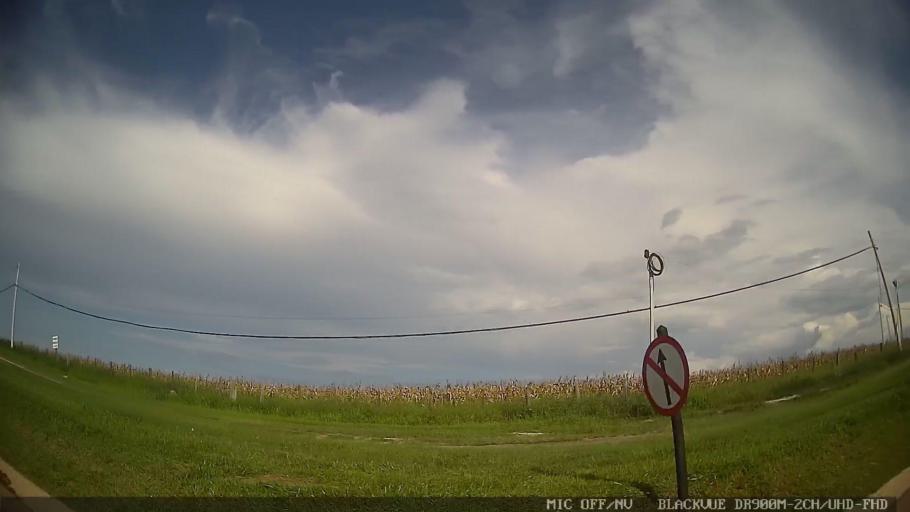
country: BR
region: Sao Paulo
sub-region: Tiete
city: Tiete
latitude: -23.1190
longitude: -47.7001
